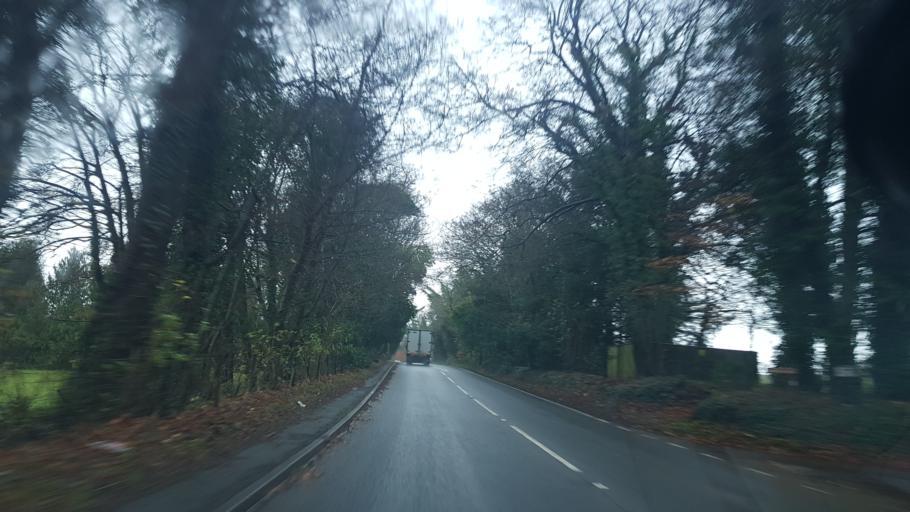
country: GB
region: England
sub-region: Surrey
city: East Horsley
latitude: 51.2633
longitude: -0.4083
